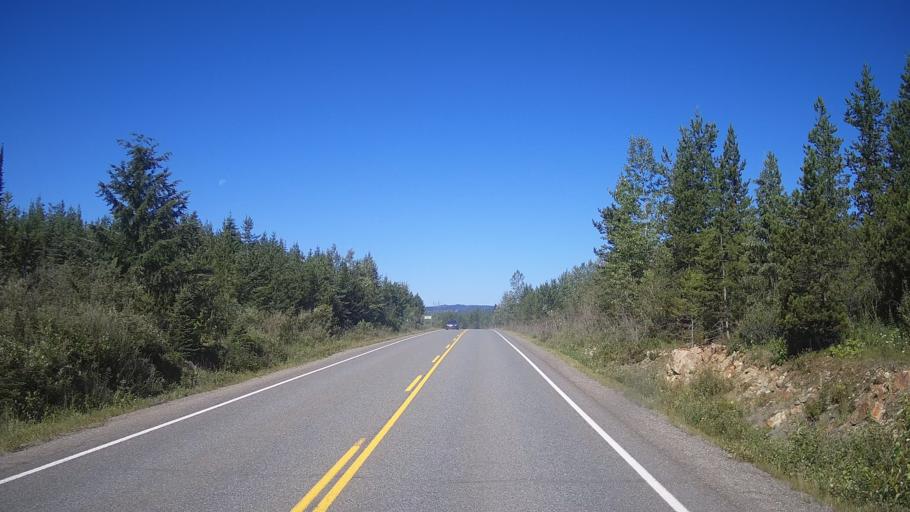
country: CA
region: British Columbia
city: Kamloops
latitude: 51.4962
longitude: -120.3988
